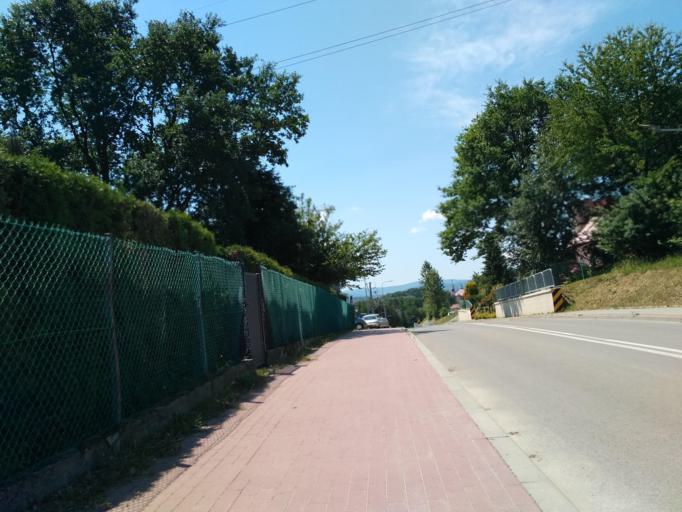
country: PL
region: Subcarpathian Voivodeship
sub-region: Krosno
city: Krosno
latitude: 49.7061
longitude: 21.7805
